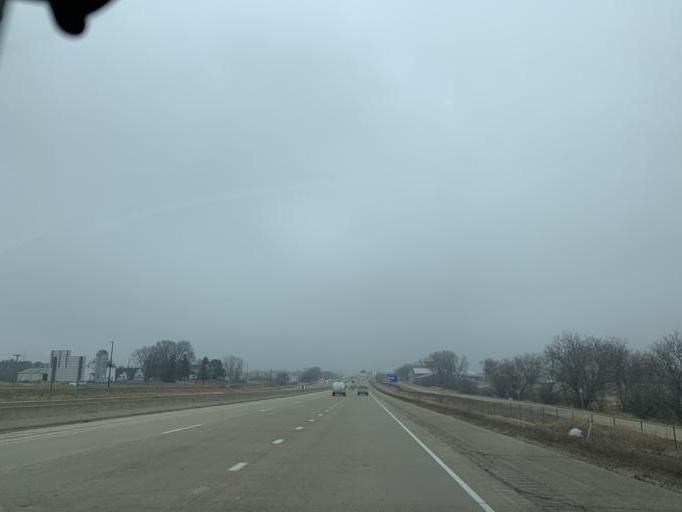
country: US
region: Wisconsin
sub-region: Dane County
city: Sun Prairie
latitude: 43.1697
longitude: -89.2572
